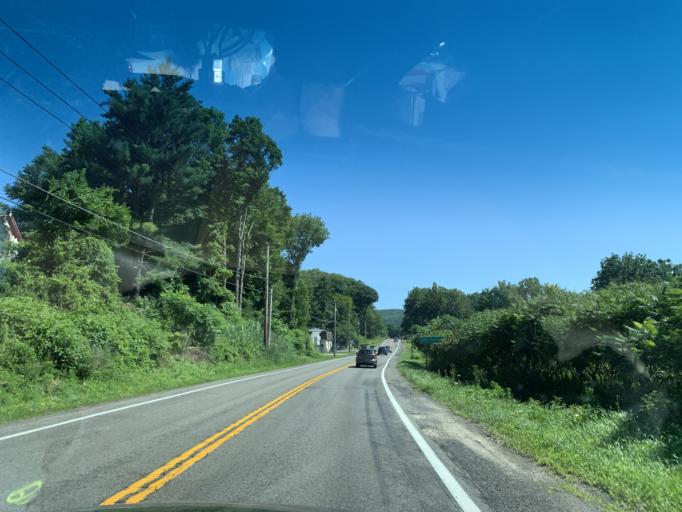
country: US
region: New York
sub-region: Delaware County
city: Sidney
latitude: 42.3364
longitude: -75.4073
